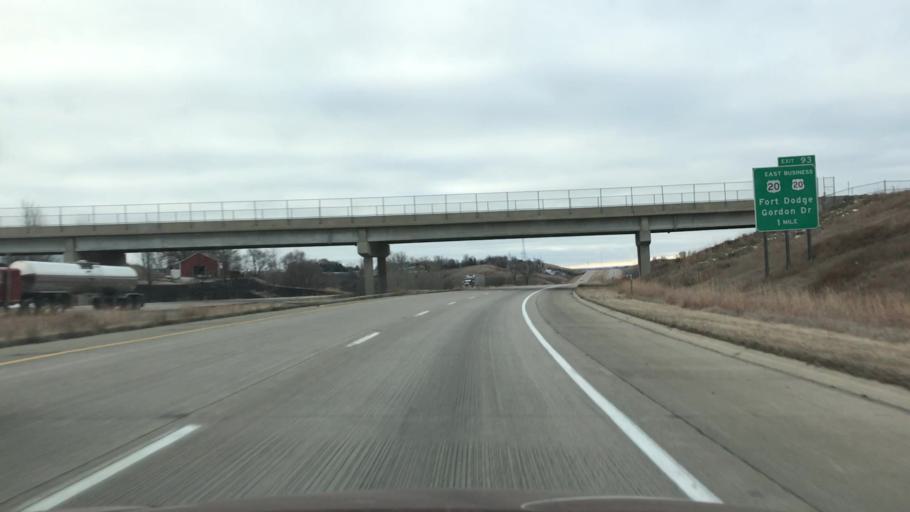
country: US
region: Iowa
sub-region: Woodbury County
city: Sioux City
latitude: 42.4977
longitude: -96.3199
